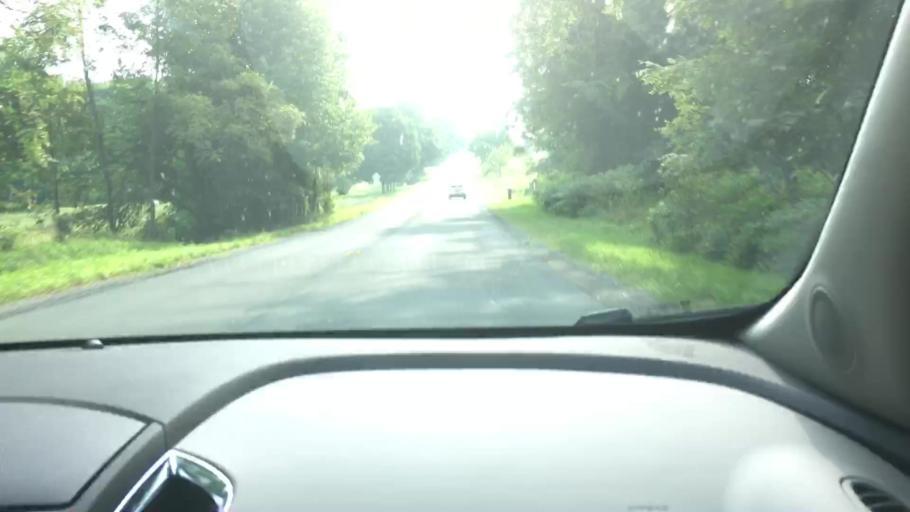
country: US
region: Michigan
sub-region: Kalamazoo County
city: Schoolcraft
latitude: 42.0273
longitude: -85.7033
